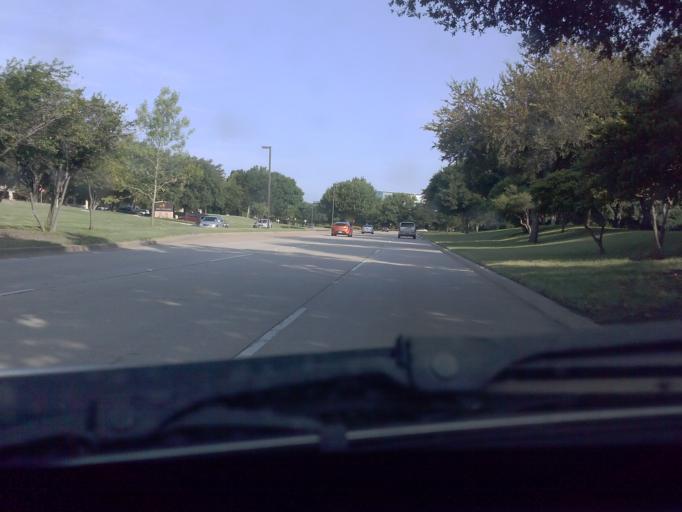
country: US
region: Texas
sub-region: Denton County
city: The Colony
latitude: 33.0688
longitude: -96.8082
